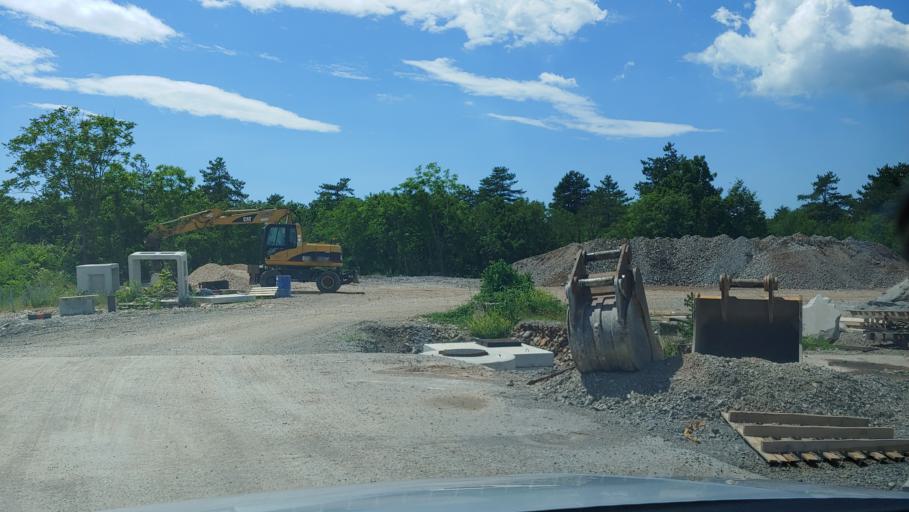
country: SI
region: Sezana
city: Sezana
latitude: 45.6993
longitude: 13.8451
